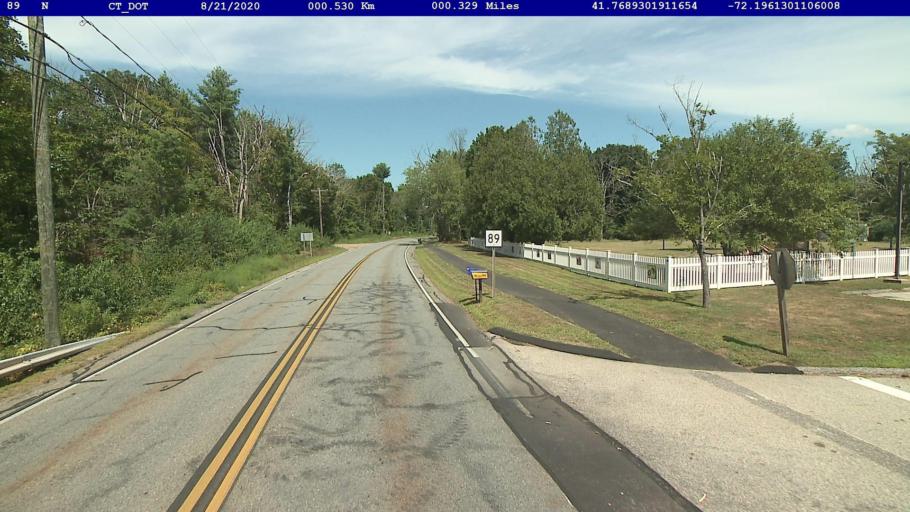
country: US
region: Connecticut
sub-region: Tolland County
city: Mansfield City
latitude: 41.7689
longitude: -72.1961
